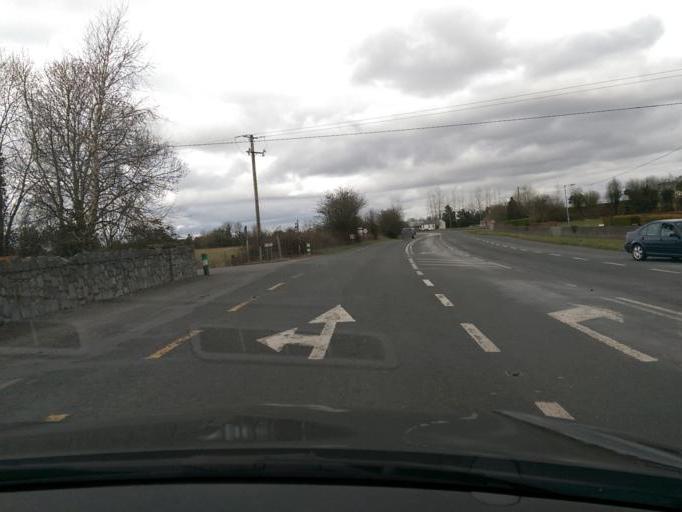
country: IE
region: Leinster
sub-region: An Iarmhi
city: Athlone
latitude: 53.3759
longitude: -8.0054
